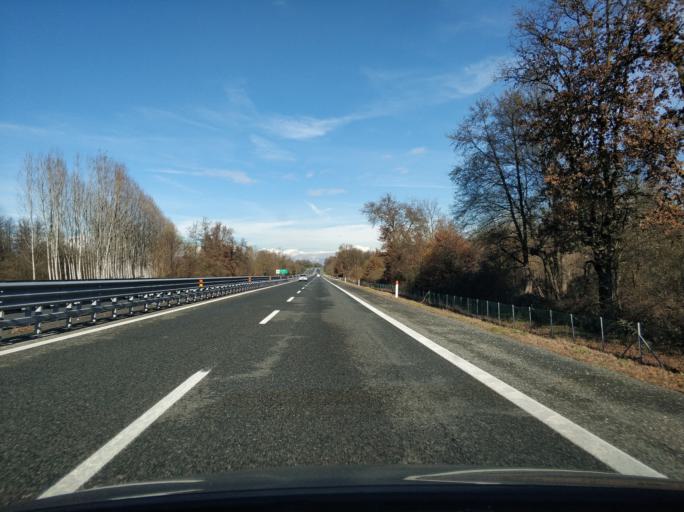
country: IT
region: Piedmont
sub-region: Provincia di Torino
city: Foglizzo
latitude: 45.2913
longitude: 7.8155
